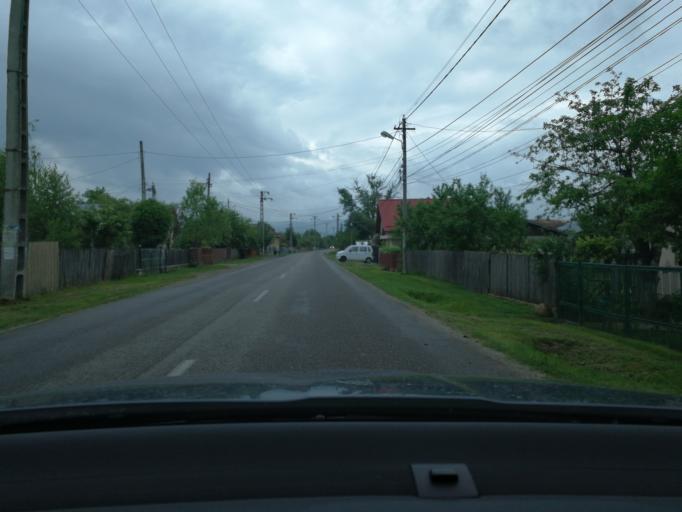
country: RO
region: Prahova
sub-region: Comuna Brebu
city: Brebu Megiesesc
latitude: 45.1545
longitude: 25.7738
